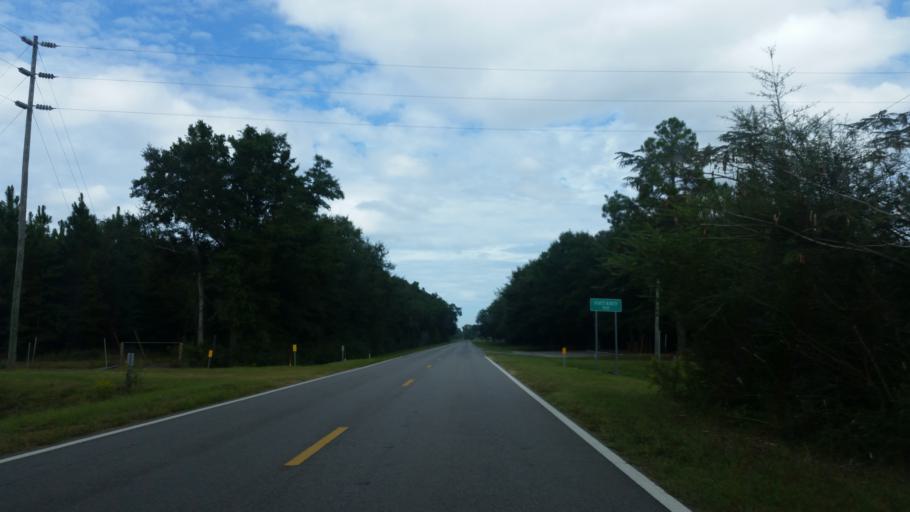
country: US
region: Florida
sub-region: Santa Rosa County
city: Point Baker
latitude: 30.6955
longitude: -86.9933
